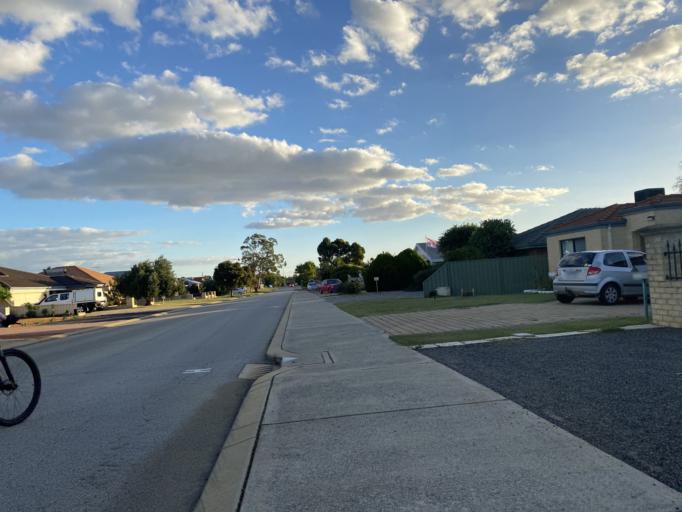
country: AU
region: Western Australia
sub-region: Kalamunda
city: Maida Vale
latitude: -31.9703
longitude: 116.0057
